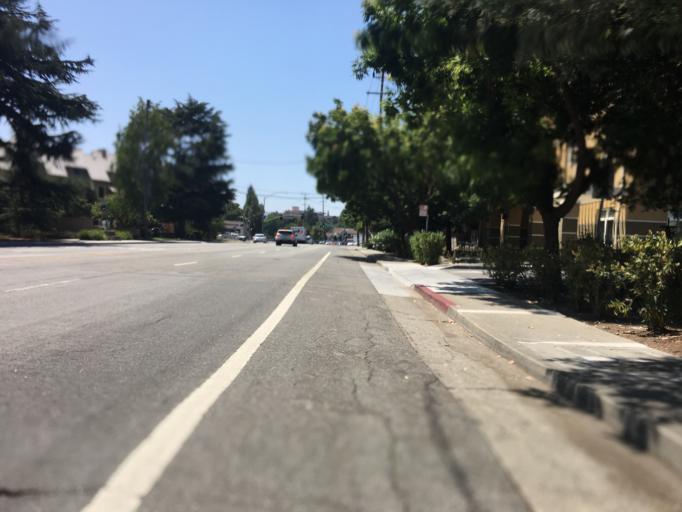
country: US
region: California
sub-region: Santa Clara County
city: Los Altos
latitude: 37.4115
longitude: -122.1222
